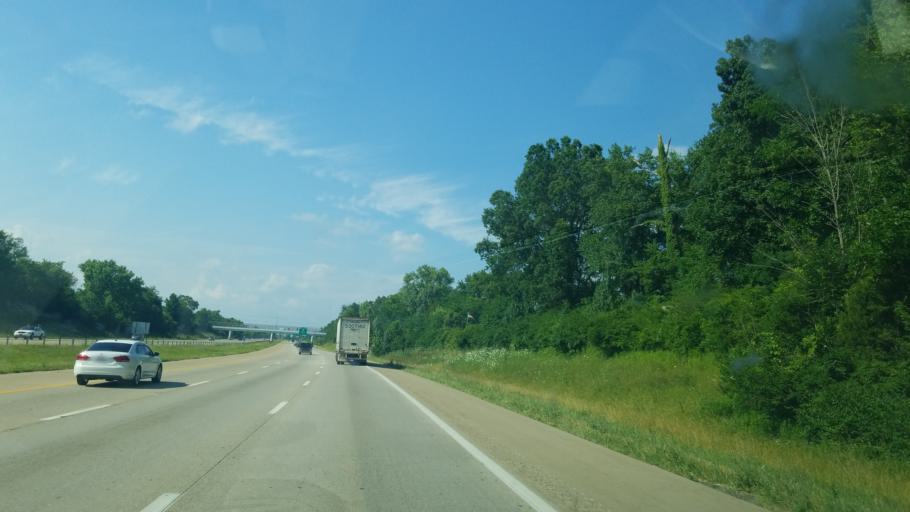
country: US
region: Ohio
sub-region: Clermont County
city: Withamsville
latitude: 39.0808
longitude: -84.2903
